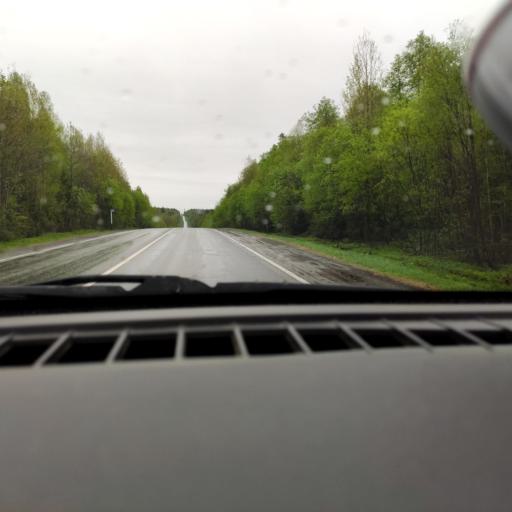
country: RU
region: Perm
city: Perm
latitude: 58.1697
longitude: 56.2359
